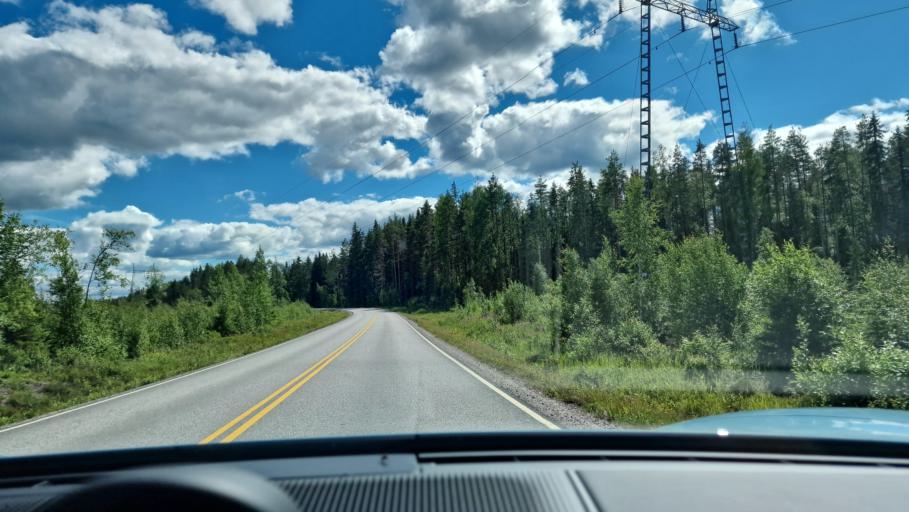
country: FI
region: Central Finland
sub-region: Saarijaervi-Viitasaari
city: Pylkoenmaeki
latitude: 62.6492
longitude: 24.5724
